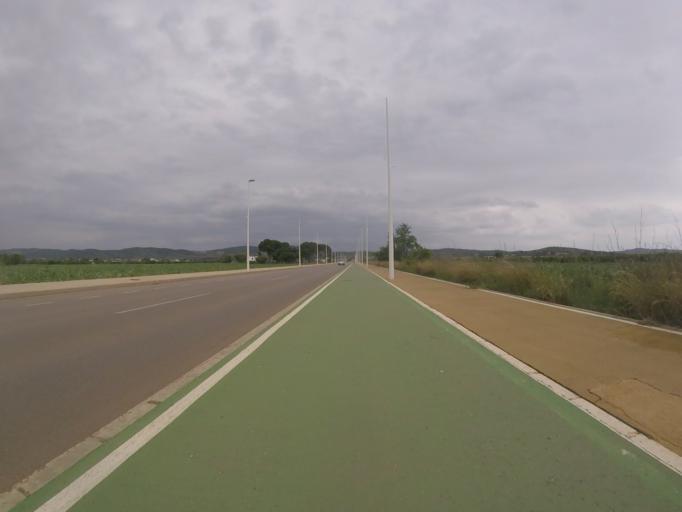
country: ES
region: Valencia
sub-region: Provincia de Castello
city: Torreblanca
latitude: 40.2200
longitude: 0.2165
